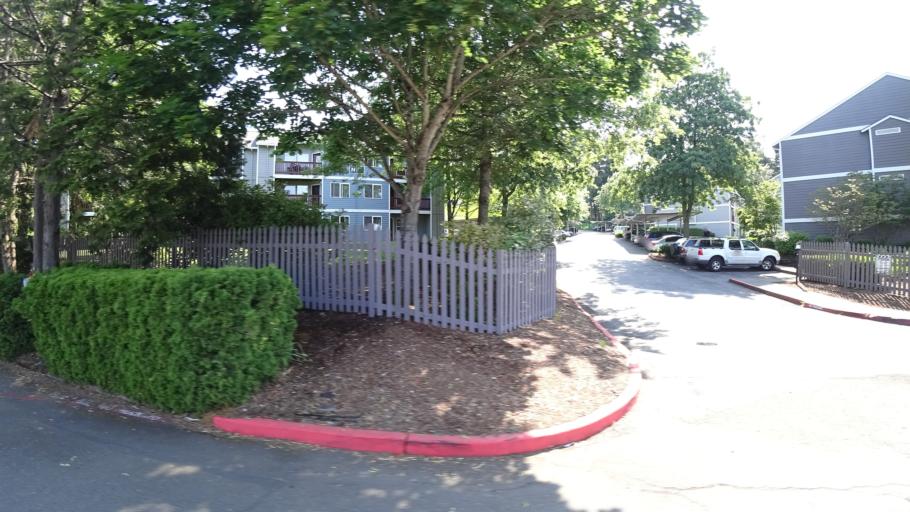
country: US
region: Oregon
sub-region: Clackamas County
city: Oatfield
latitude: 45.4485
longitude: -122.5953
